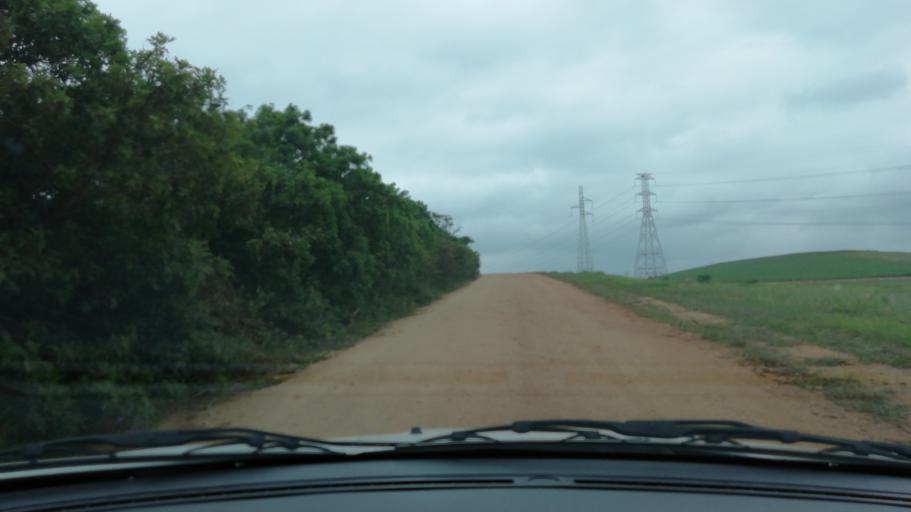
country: ZA
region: KwaZulu-Natal
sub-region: uThungulu District Municipality
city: Empangeni
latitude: -28.7296
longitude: 31.9066
